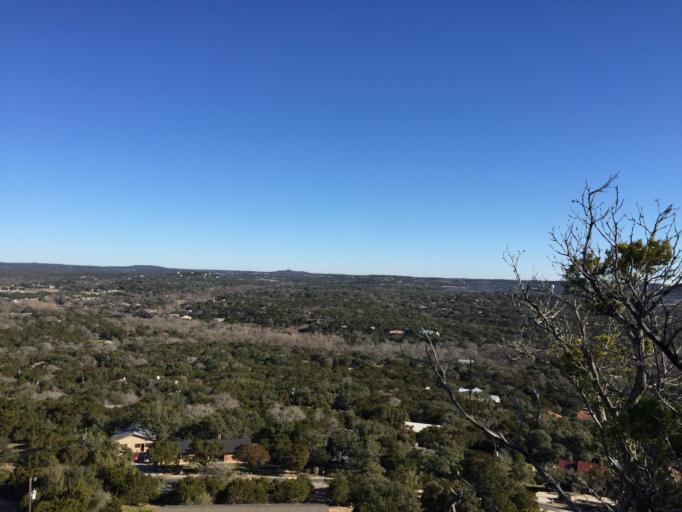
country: US
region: Texas
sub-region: Hays County
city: Woodcreek
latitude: 30.0099
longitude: -98.1161
